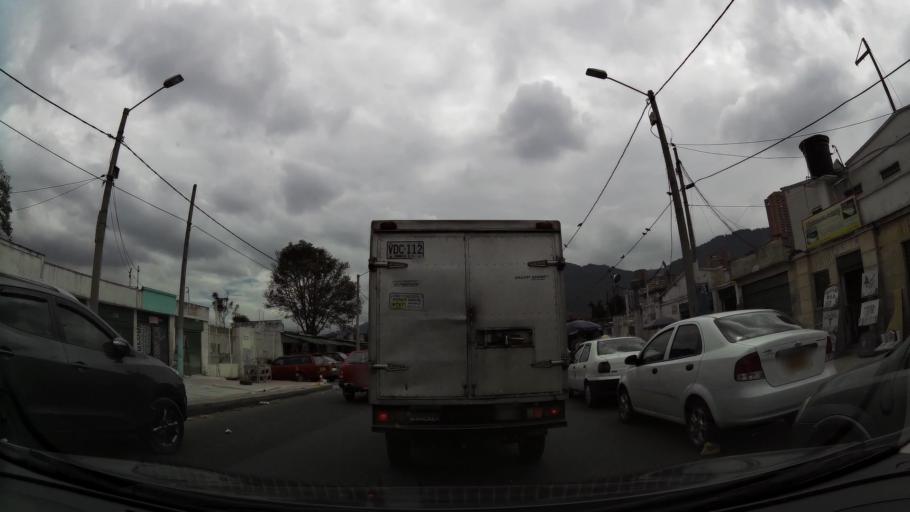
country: CO
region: Bogota D.C.
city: Bogota
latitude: 4.6173
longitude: -74.0764
